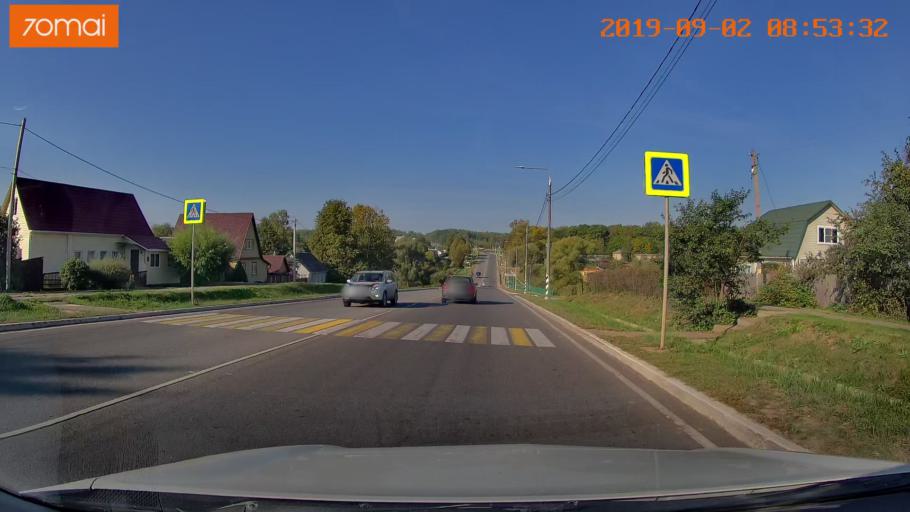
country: RU
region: Kaluga
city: Medyn'
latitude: 54.9660
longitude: 35.8548
